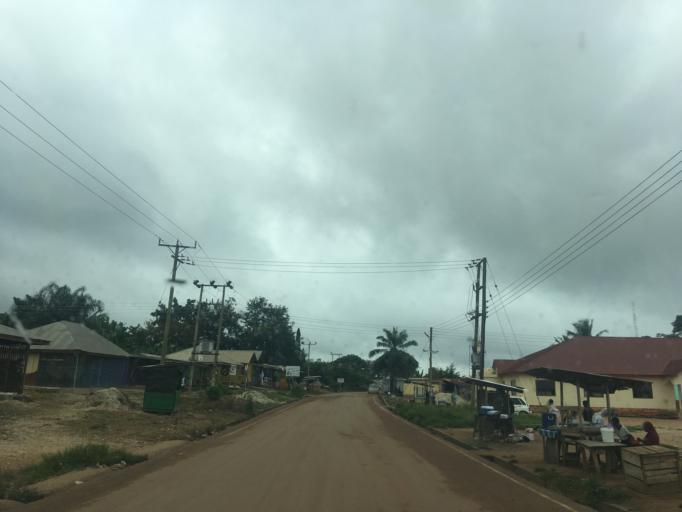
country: GH
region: Western
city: Wassa-Akropong
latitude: 5.8157
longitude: -2.4342
